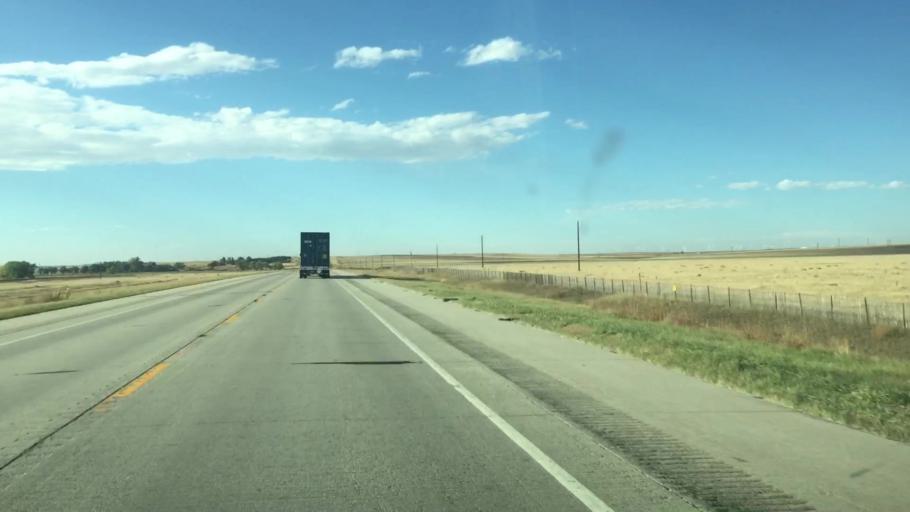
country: US
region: Colorado
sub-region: Lincoln County
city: Limon
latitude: 39.2304
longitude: -103.6161
